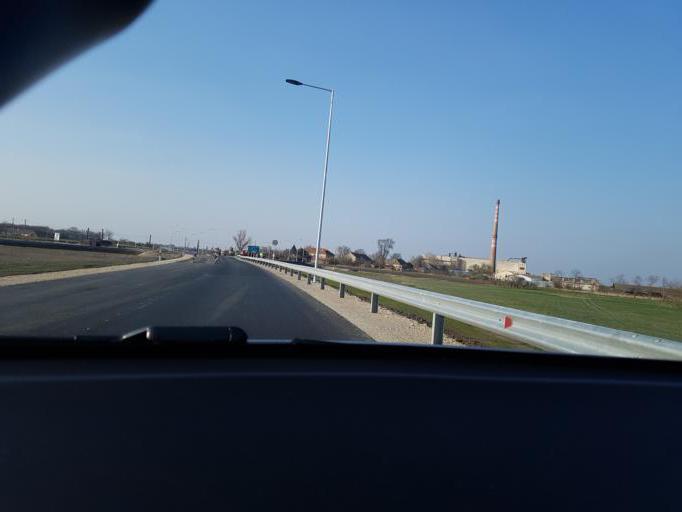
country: RO
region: Arad
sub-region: Comuna Nadlac
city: Nadlac
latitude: 46.1846
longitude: 20.7186
